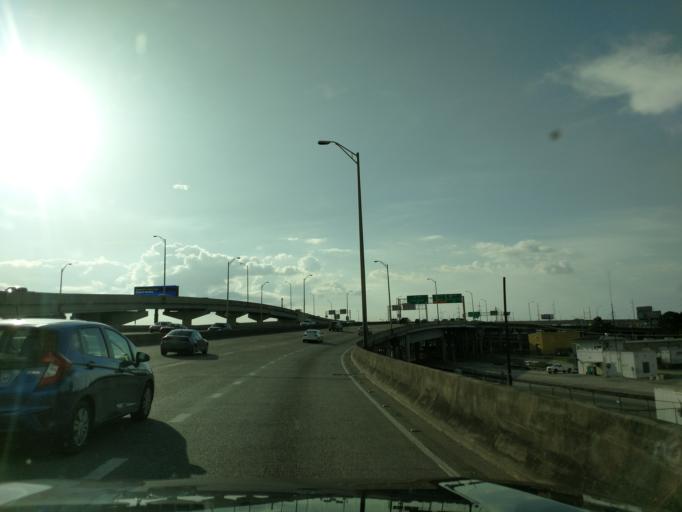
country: US
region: Louisiana
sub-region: Orleans Parish
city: New Orleans
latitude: 29.9484
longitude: -90.0836
